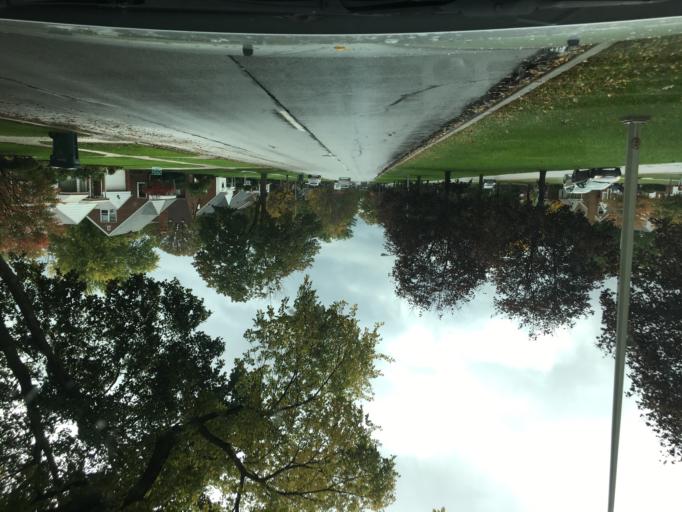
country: US
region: Michigan
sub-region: Wayne County
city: Allen Park
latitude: 42.2808
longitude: -83.2241
